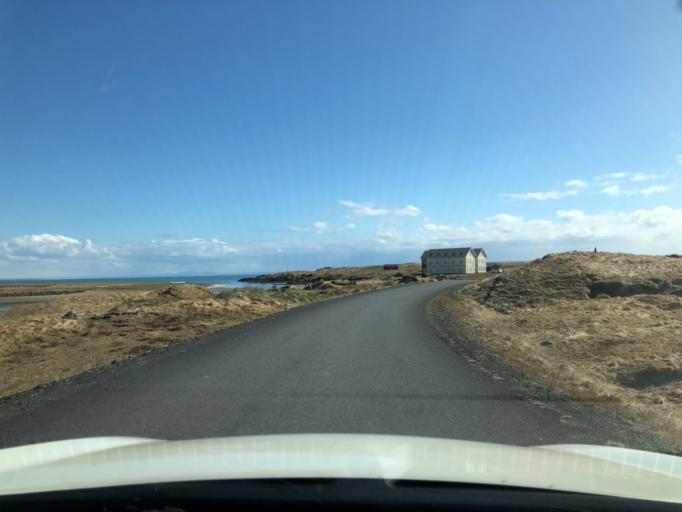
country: IS
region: West
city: Olafsvik
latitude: 64.8250
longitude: -23.3874
